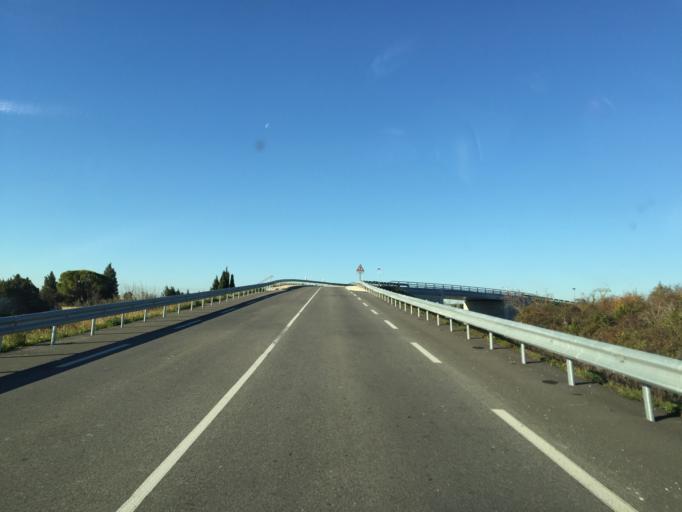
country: FR
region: Provence-Alpes-Cote d'Azur
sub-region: Departement du Vaucluse
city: Entraigues-sur-la-Sorgue
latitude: 44.0099
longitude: 4.9366
